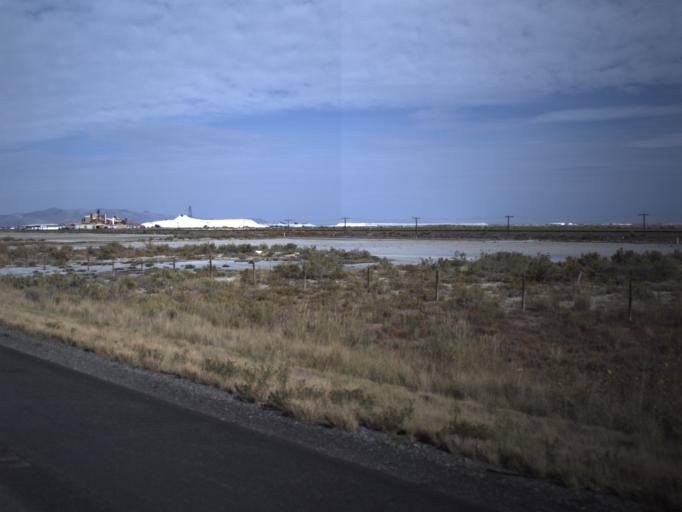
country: US
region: Utah
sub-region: Tooele County
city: Grantsville
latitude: 40.7025
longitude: -112.4962
